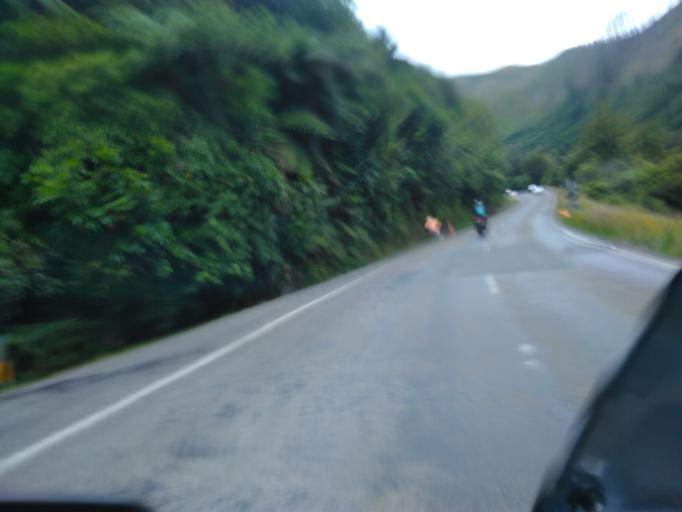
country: NZ
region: Bay of Plenty
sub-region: Opotiki District
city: Opotiki
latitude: -38.2639
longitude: 177.3050
